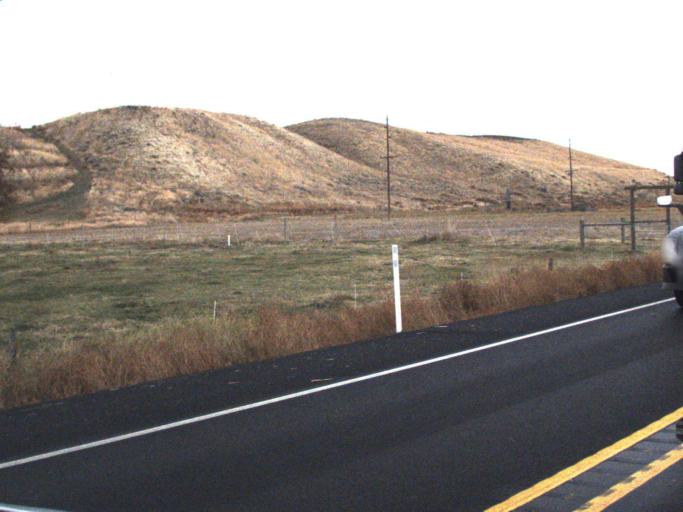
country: US
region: Washington
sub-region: Walla Walla County
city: Garrett
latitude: 46.0556
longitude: -118.5787
